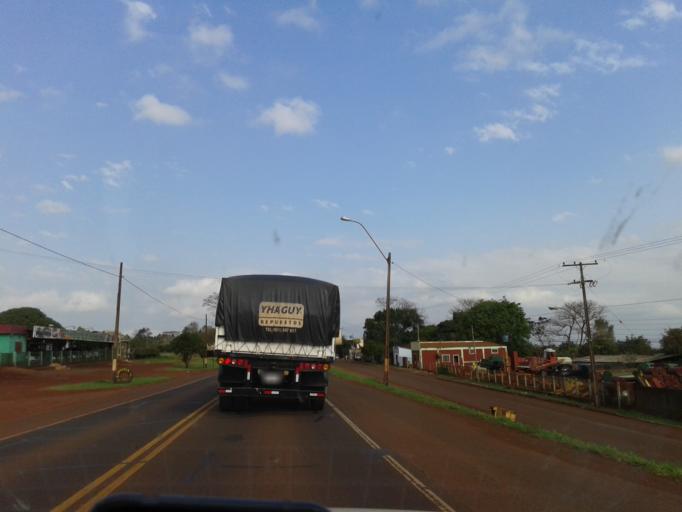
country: PY
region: Itapua
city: Arquitecto Tomas Romero Pereira
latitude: -26.5045
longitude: -55.2767
